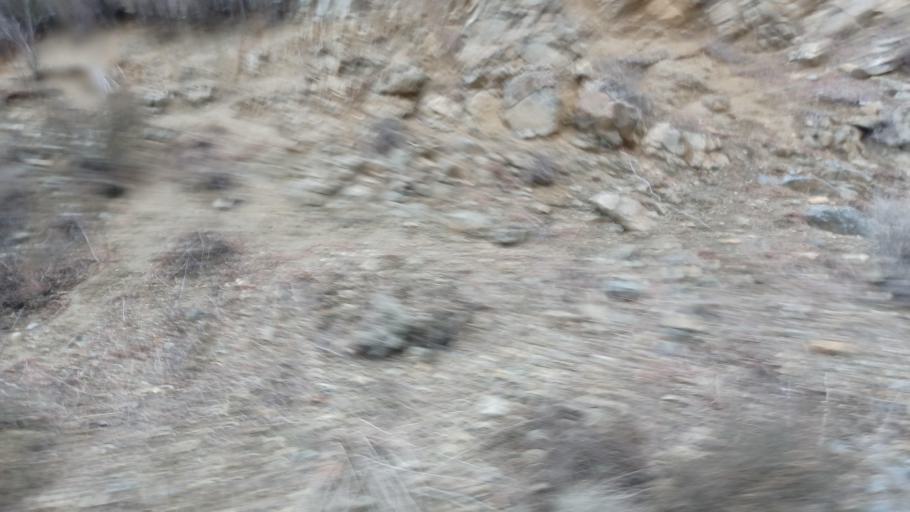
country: CY
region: Limassol
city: Kyperounta
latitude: 34.9292
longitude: 32.9712
